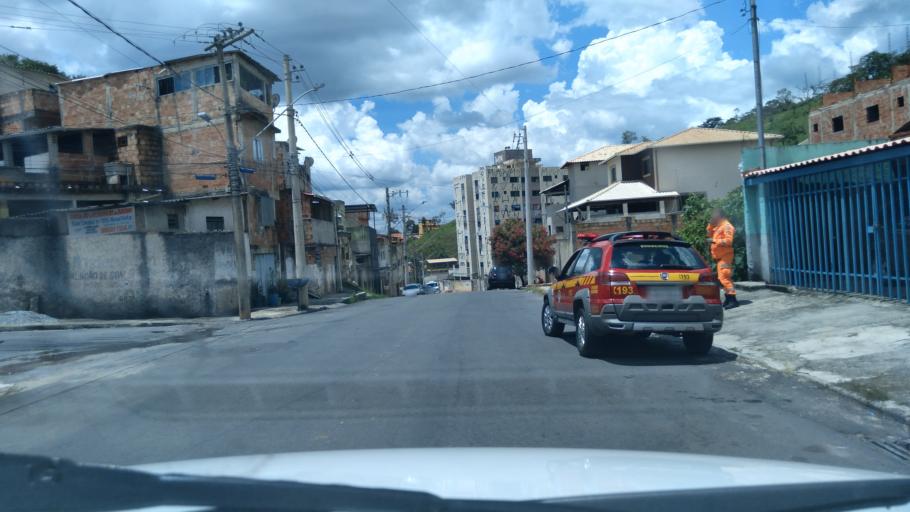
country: BR
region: Minas Gerais
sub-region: Belo Horizonte
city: Belo Horizonte
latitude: -19.8837
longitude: -43.8943
